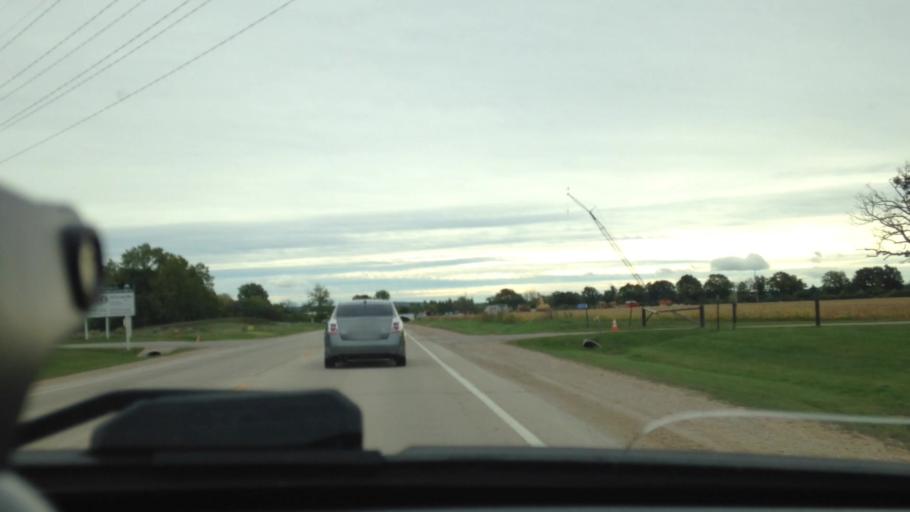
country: US
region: Wisconsin
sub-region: Fond du Lac County
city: North Fond du Lac
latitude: 43.7995
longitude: -88.4932
